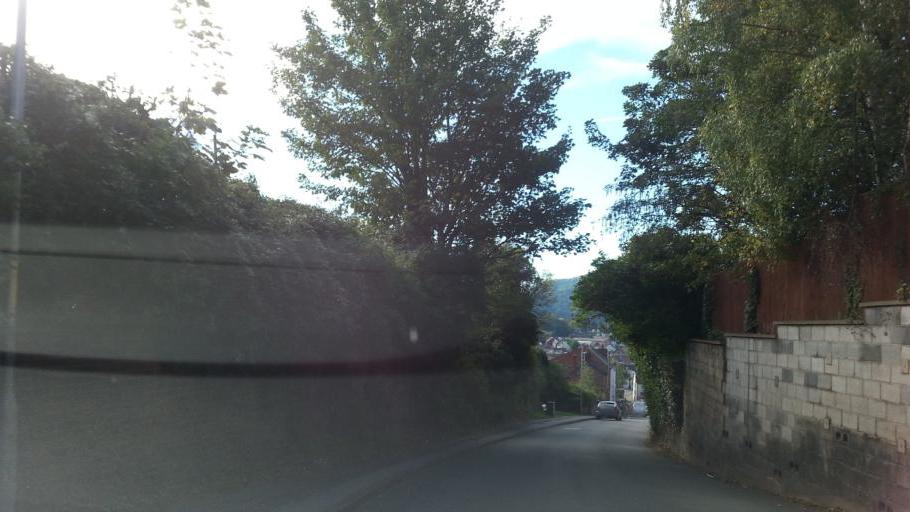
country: GB
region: England
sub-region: Herefordshire
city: Ross on Wye
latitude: 51.9198
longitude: -2.5813
